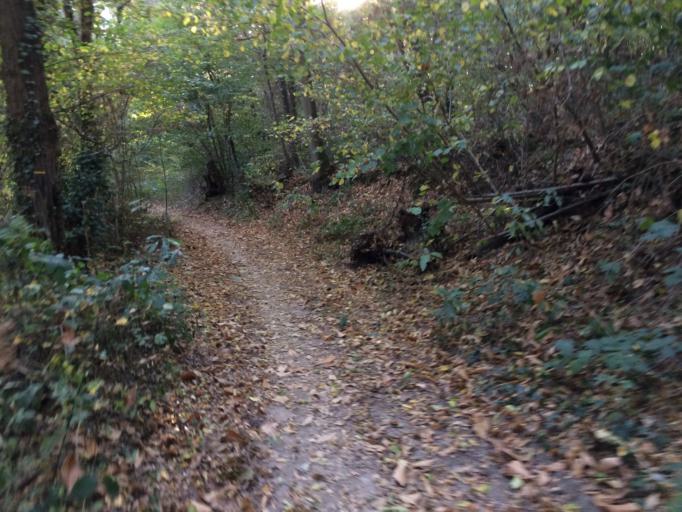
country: FR
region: Ile-de-France
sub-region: Departement de l'Essonne
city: Villejust
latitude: 48.6868
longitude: 2.2412
